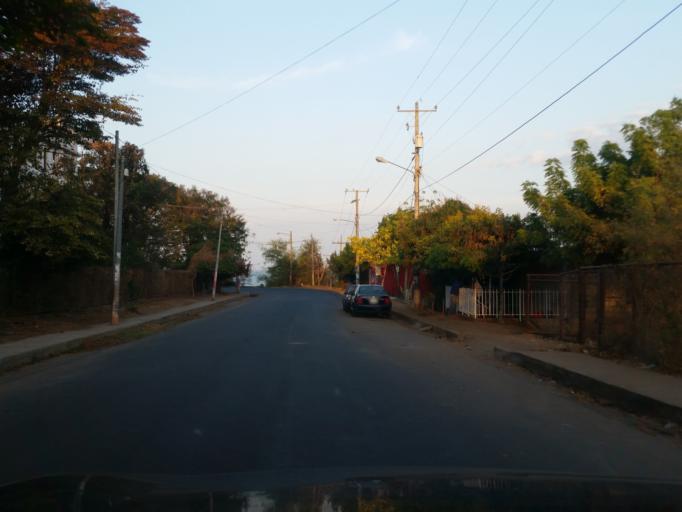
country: NI
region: Granada
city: Granada
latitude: 11.9408
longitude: -85.9465
